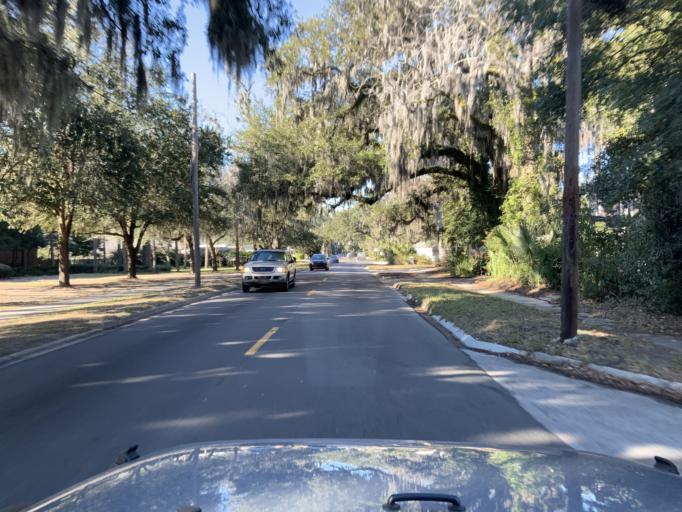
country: US
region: Georgia
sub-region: Chatham County
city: Thunderbolt
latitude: 32.0533
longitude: -81.0671
